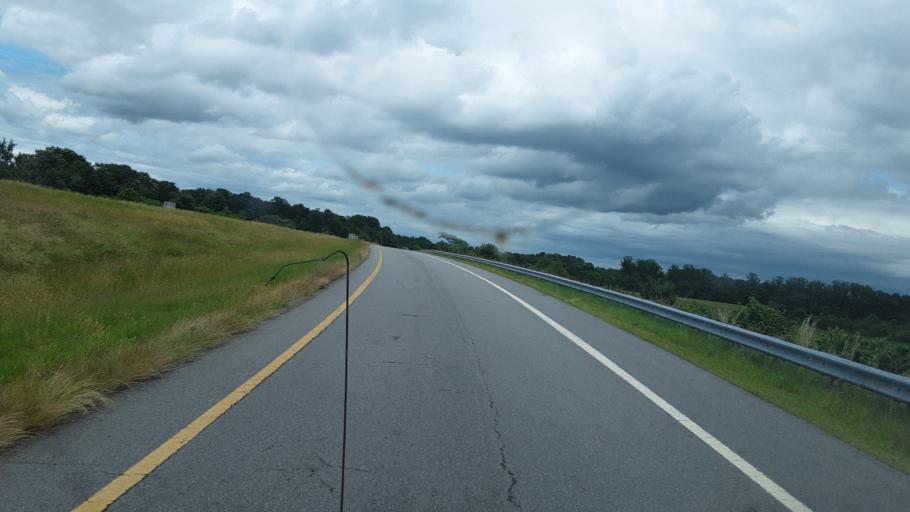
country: US
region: North Carolina
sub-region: Yadkin County
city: Yadkinville
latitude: 36.1156
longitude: -80.7704
